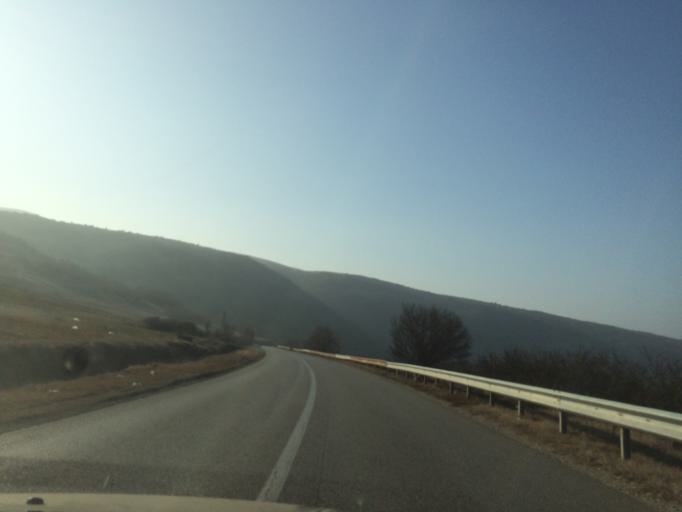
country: XK
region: Pec
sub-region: Komuna e Pejes
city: Kosuriq
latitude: 42.5119
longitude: 20.5472
